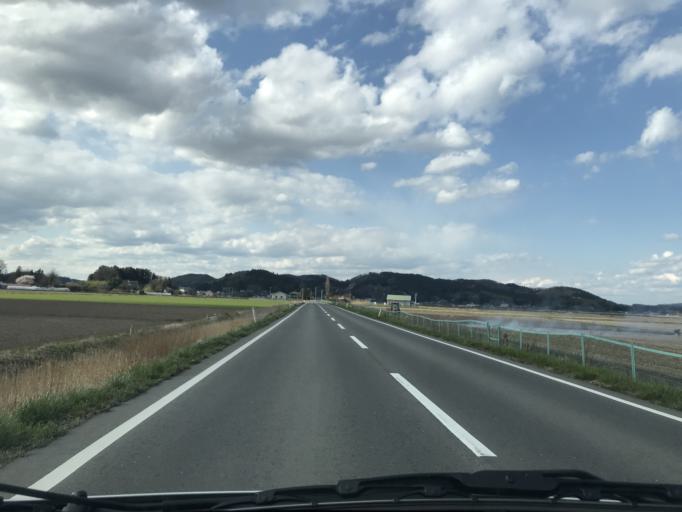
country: JP
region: Iwate
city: Ichinoseki
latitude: 38.7345
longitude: 141.2284
